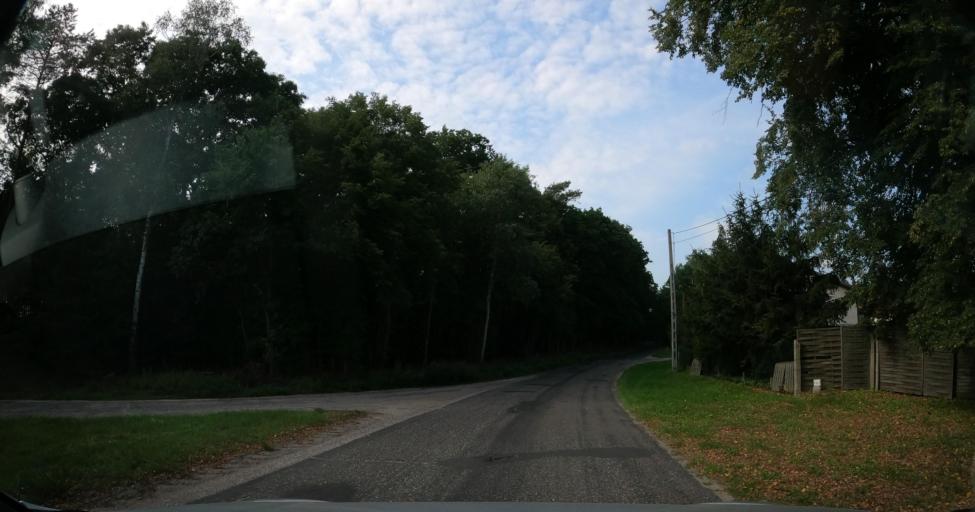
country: PL
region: West Pomeranian Voivodeship
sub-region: Powiat goleniowski
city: Goleniow
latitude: 53.5071
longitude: 14.8670
